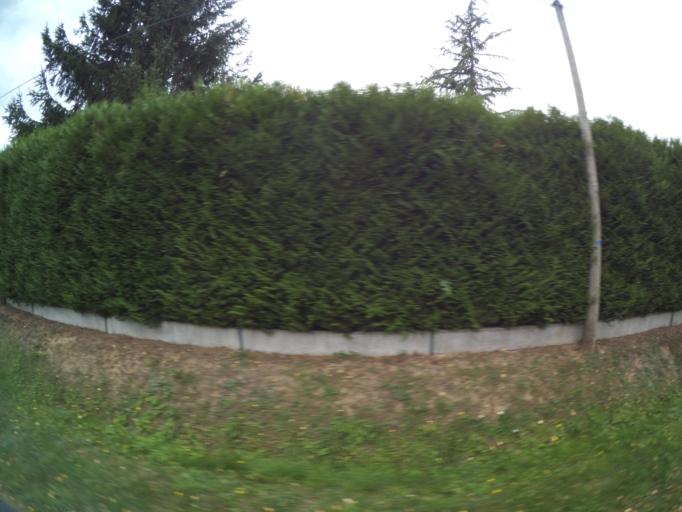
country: FR
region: Centre
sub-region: Departement d'Indre-et-Loire
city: Poce-sur-Cisse
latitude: 47.4949
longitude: 0.9840
